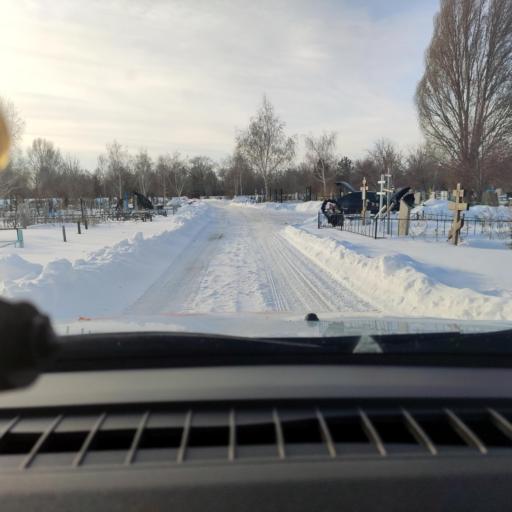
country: RU
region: Samara
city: Chapayevsk
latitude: 52.9894
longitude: 49.7477
